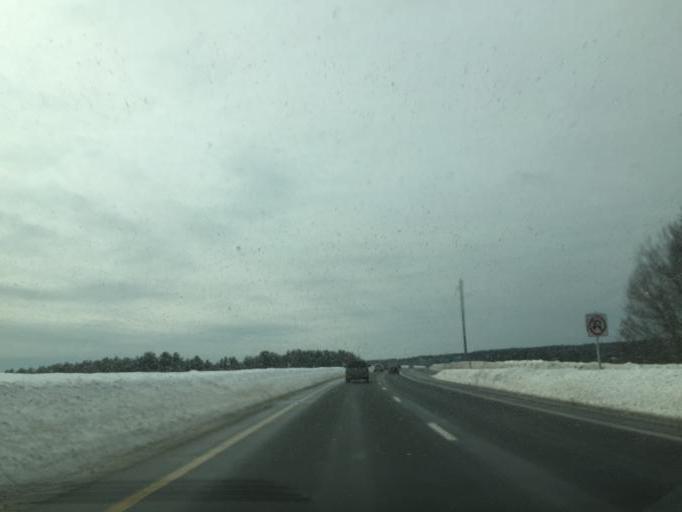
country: US
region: New Hampshire
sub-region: Strafford County
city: Rochester
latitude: 43.3283
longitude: -70.9854
